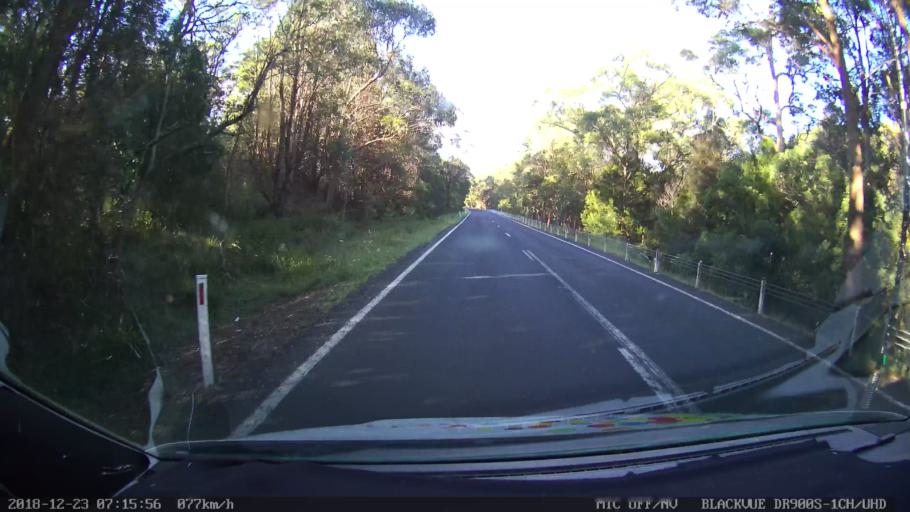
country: AU
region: New South Wales
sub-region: Bellingen
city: Dorrigo
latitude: -30.4509
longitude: 152.3135
